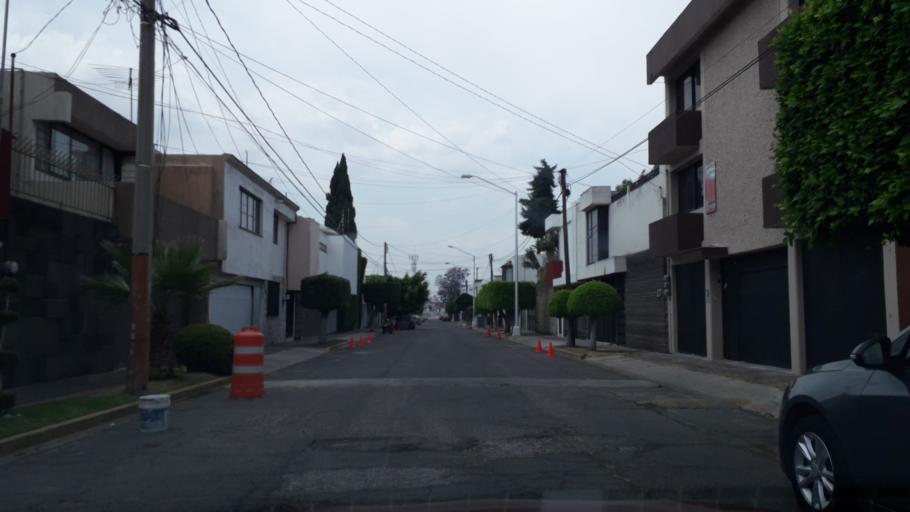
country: MX
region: Puebla
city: Puebla
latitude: 19.0212
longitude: -98.1936
